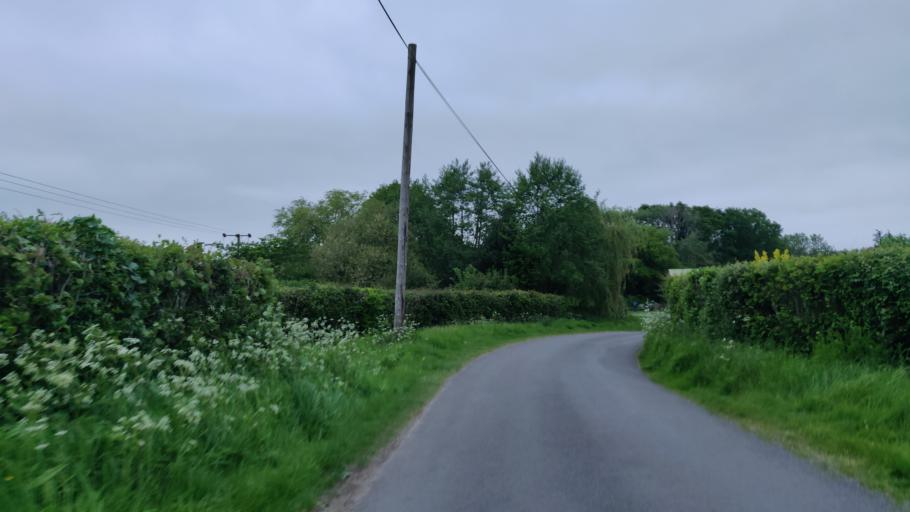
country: GB
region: England
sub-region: West Sussex
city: Southwater
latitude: 51.0328
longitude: -0.3340
